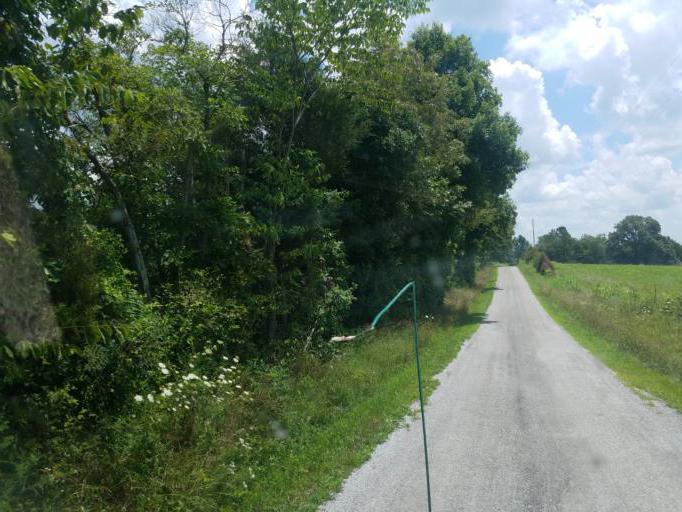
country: US
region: Kentucky
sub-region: Grayson County
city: Leitchfield
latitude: 37.4834
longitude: -86.4733
